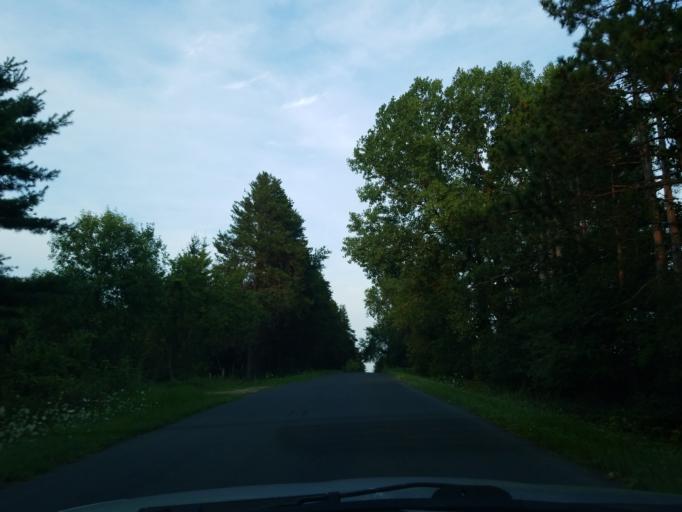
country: US
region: Minnesota
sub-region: Washington County
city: Stillwater
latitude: 45.0898
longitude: -92.7599
